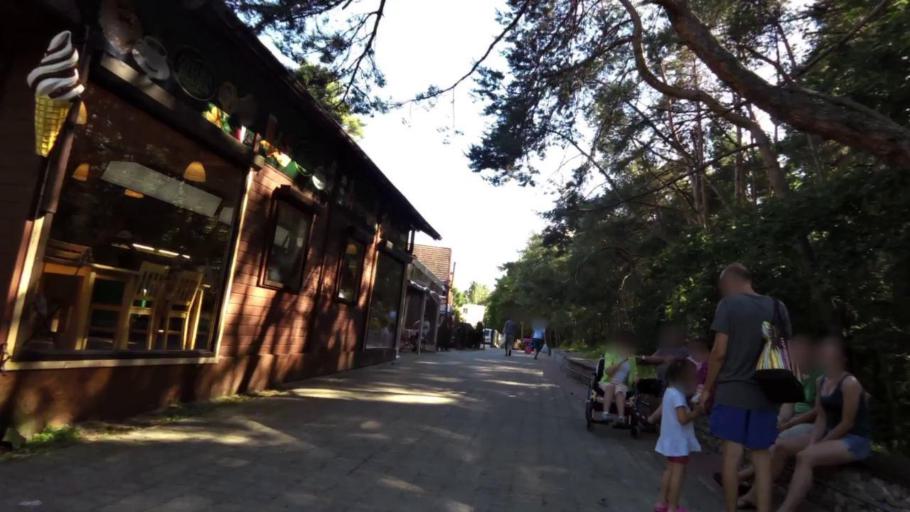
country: PL
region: West Pomeranian Voivodeship
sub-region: Powiat slawienski
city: Darlowo
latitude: 54.3809
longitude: 16.3130
